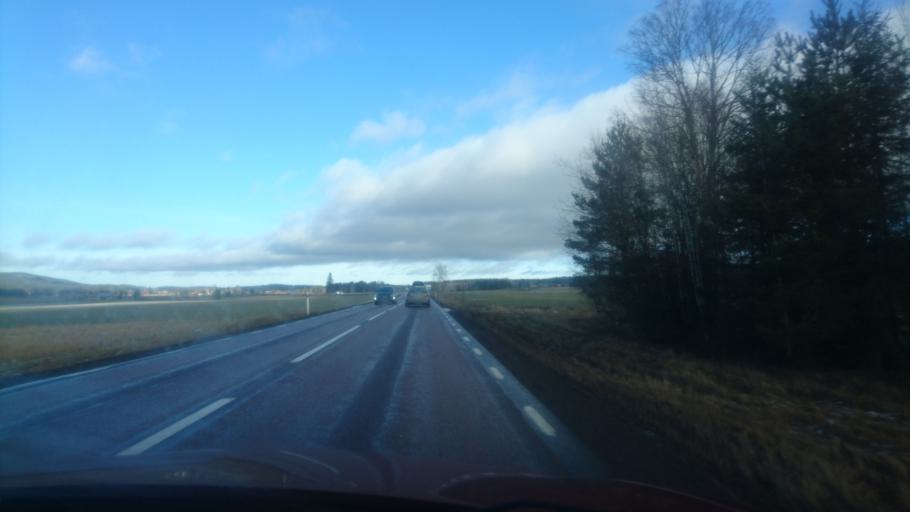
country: SE
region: Vaermland
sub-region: Sunne Kommun
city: Sunne
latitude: 59.6452
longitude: 13.1557
